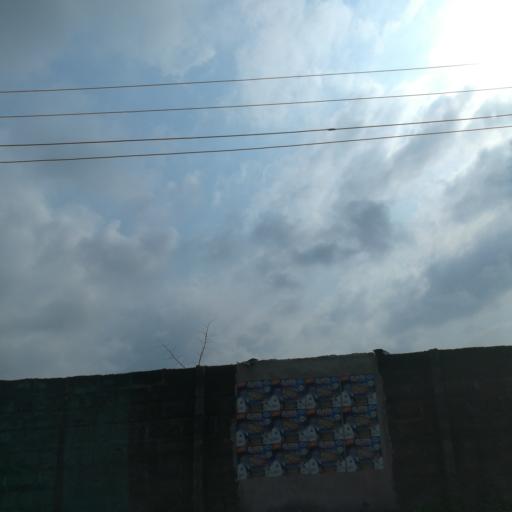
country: NG
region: Rivers
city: Okrika
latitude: 4.7821
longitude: 7.1381
